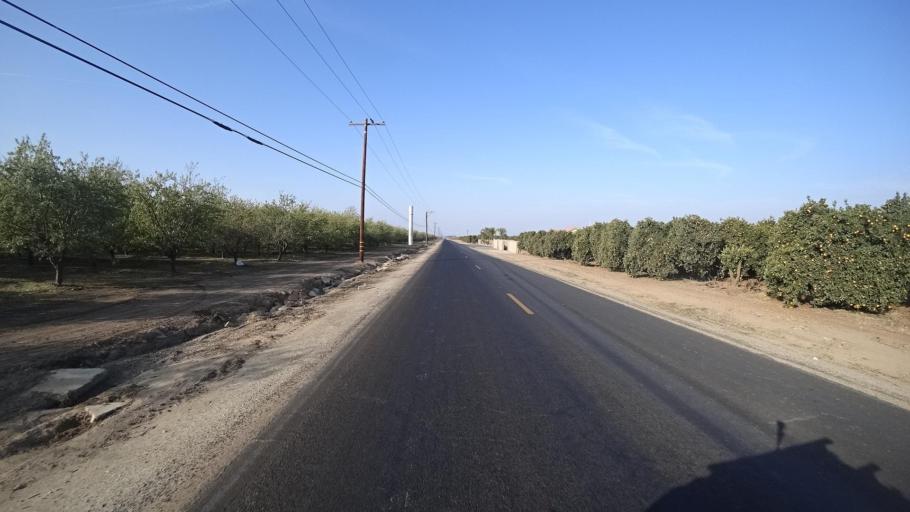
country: US
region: California
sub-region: Kern County
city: McFarland
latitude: 35.6746
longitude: -119.1528
